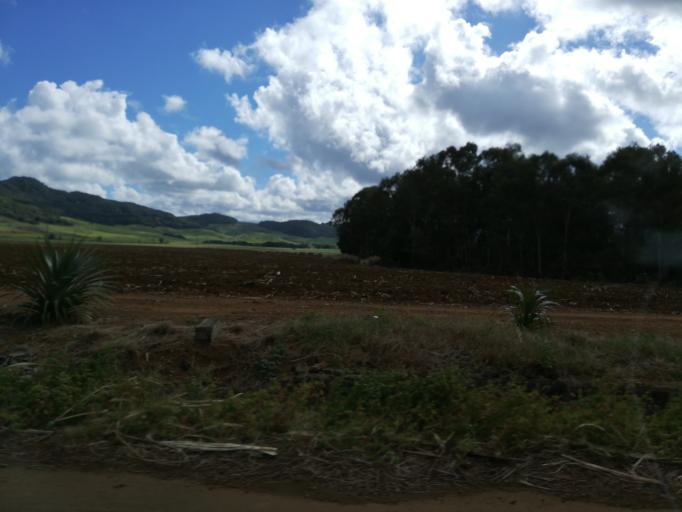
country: MU
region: Grand Port
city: Bois des Amourettes
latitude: -20.3726
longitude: 57.7004
